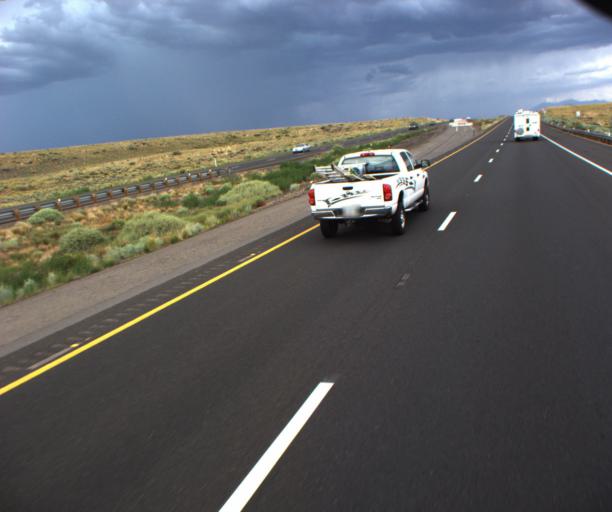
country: US
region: Arizona
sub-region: Coconino County
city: LeChee
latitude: 35.1318
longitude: -111.1907
